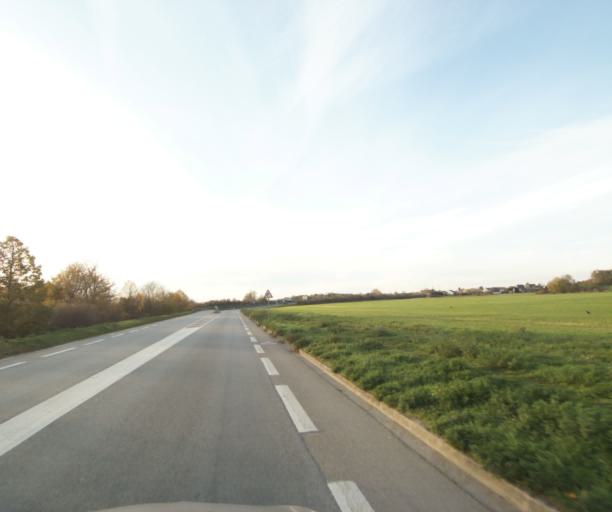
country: FR
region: Ile-de-France
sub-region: Departement des Yvelines
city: Chanteloup-les-Vignes
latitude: 48.9713
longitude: 2.0208
